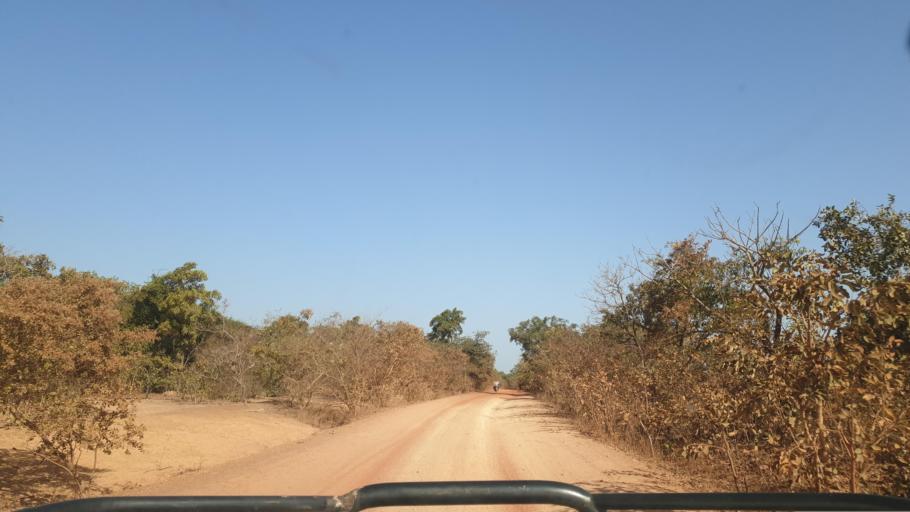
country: ML
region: Sikasso
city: Bougouni
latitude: 11.7797
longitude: -6.9079
